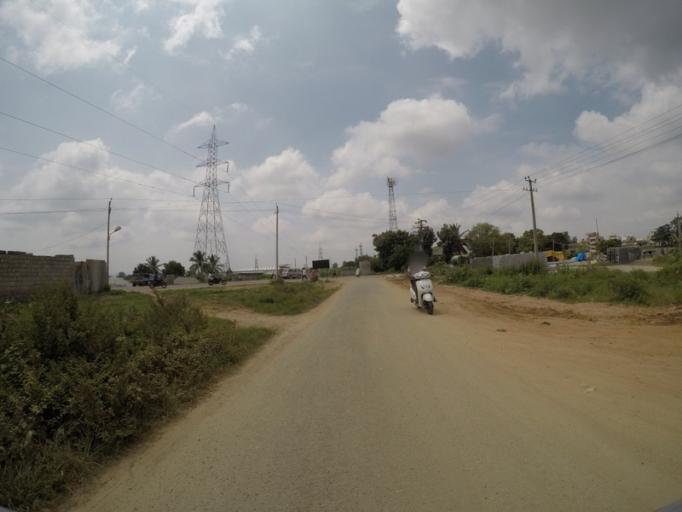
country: IN
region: Karnataka
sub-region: Bangalore Urban
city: Bangalore
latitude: 12.8492
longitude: 77.5169
